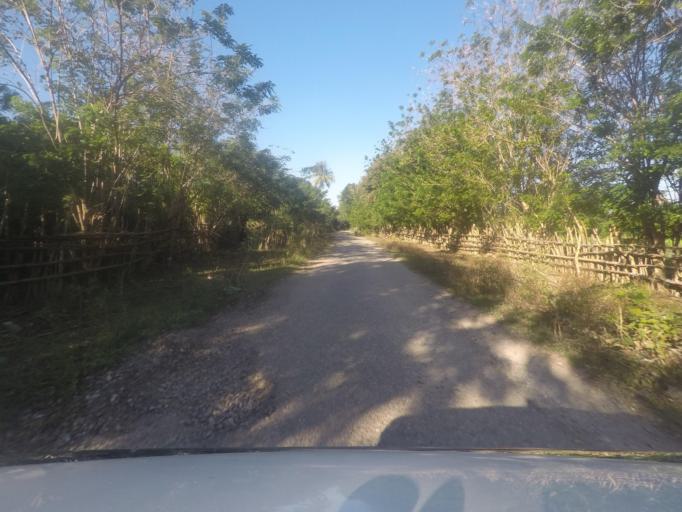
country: TL
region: Lautem
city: Lospalos
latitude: -8.4096
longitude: 127.1640
